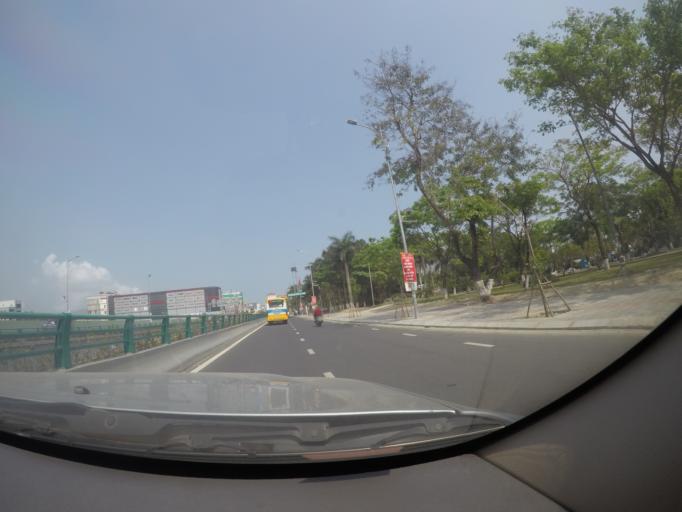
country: VN
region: Da Nang
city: Thanh Khe
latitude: 16.0658
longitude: 108.2035
